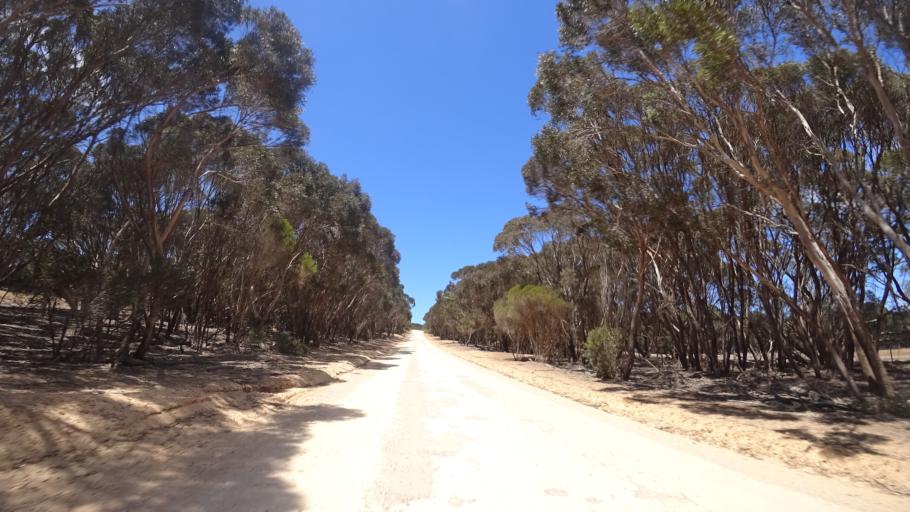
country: AU
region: South Australia
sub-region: Yankalilla
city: Normanville
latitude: -35.8269
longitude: 138.0824
